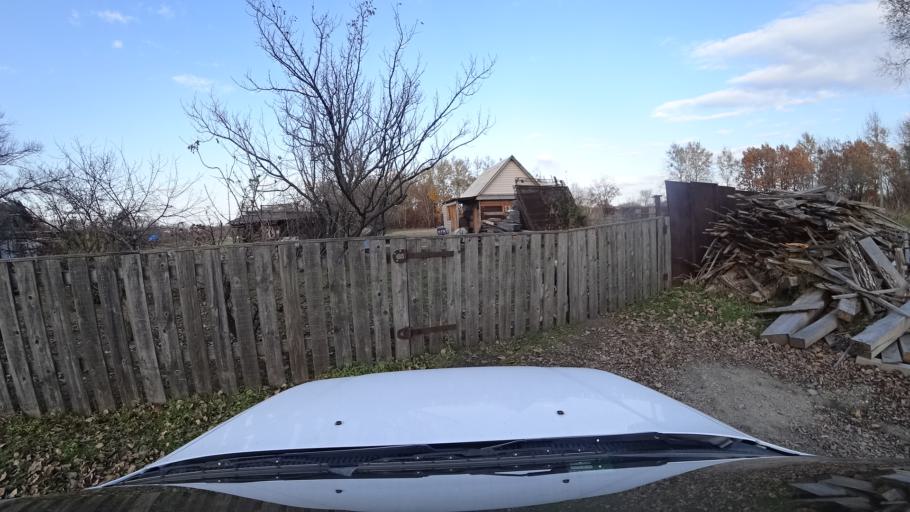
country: RU
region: Primorskiy
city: Lazo
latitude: 45.8214
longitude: 133.6167
